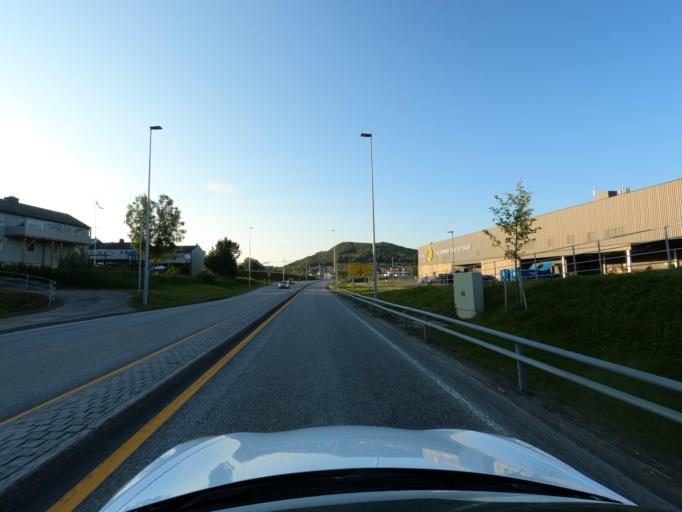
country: NO
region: Troms
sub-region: Harstad
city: Harstad
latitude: 68.7791
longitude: 16.5639
